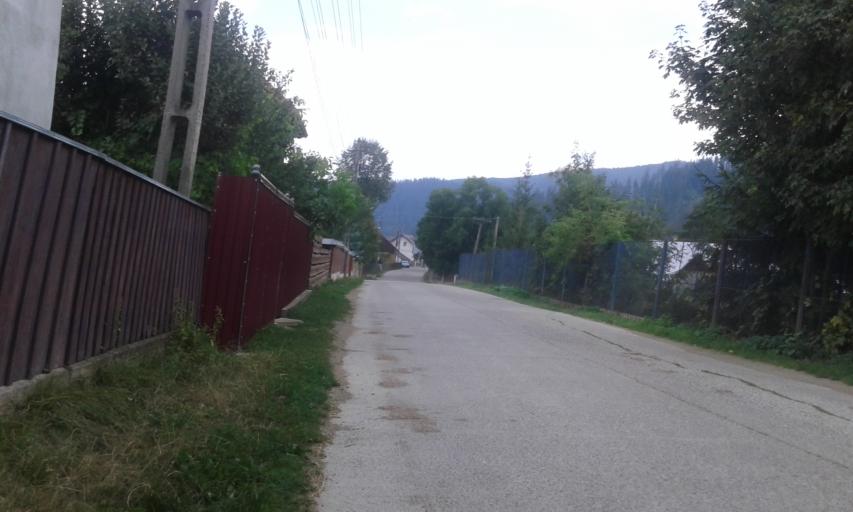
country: RO
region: Suceava
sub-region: Comuna Putna
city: Putna
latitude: 47.8670
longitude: 25.6090
